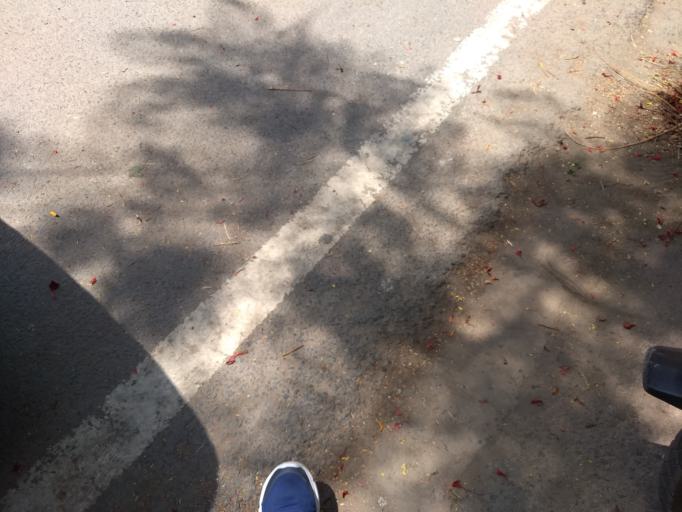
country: IN
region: NCT
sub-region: New Delhi
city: New Delhi
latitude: 28.5401
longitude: 77.2086
